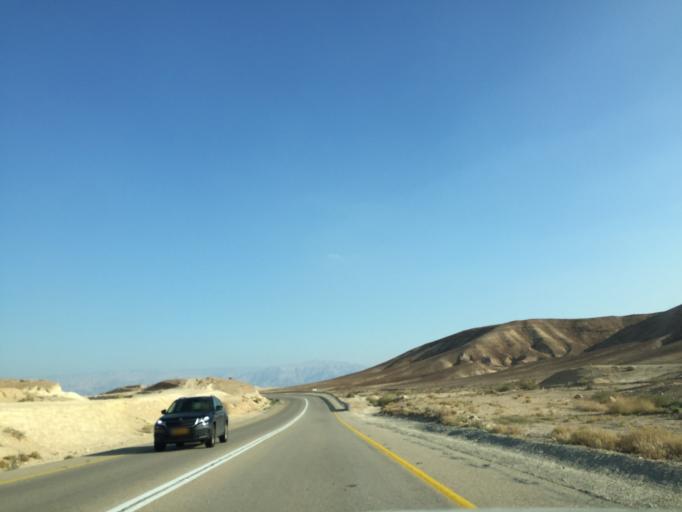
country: IL
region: Southern District
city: `En Boqeq
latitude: 31.1743
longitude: 35.3056
